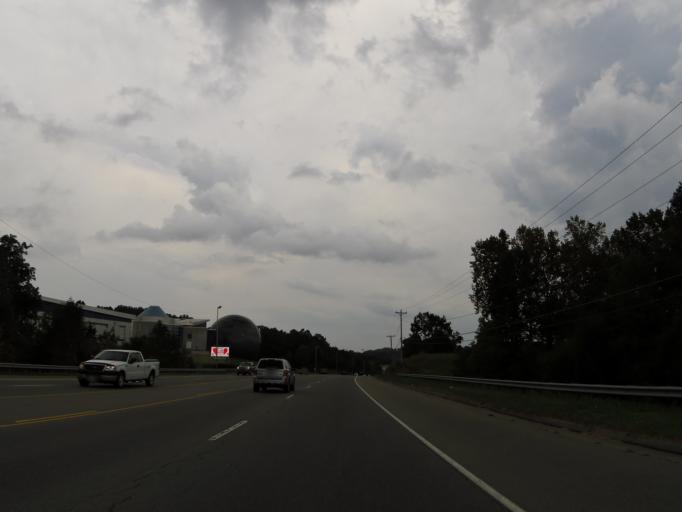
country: US
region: Tennessee
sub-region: Dickson County
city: Dickson
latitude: 36.0467
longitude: -87.3613
